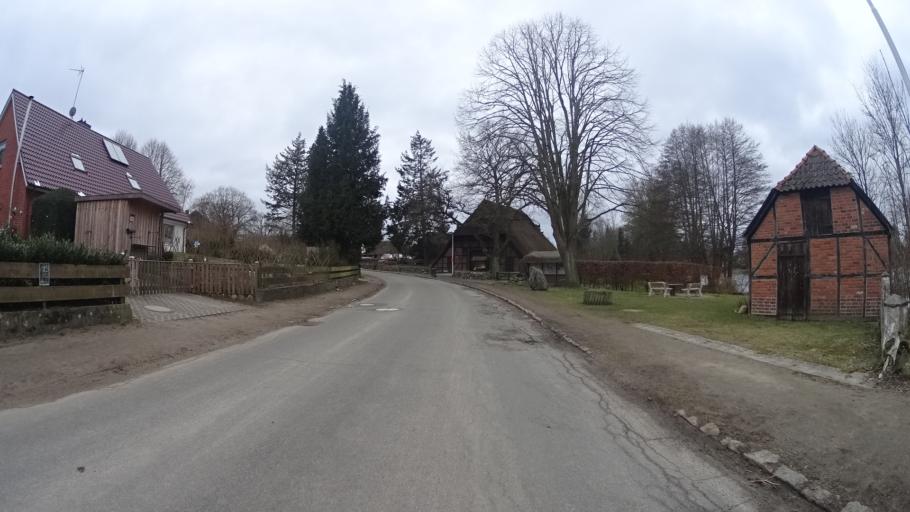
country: DE
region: Schleswig-Holstein
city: Bosdorf
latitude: 54.1718
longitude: 10.4943
